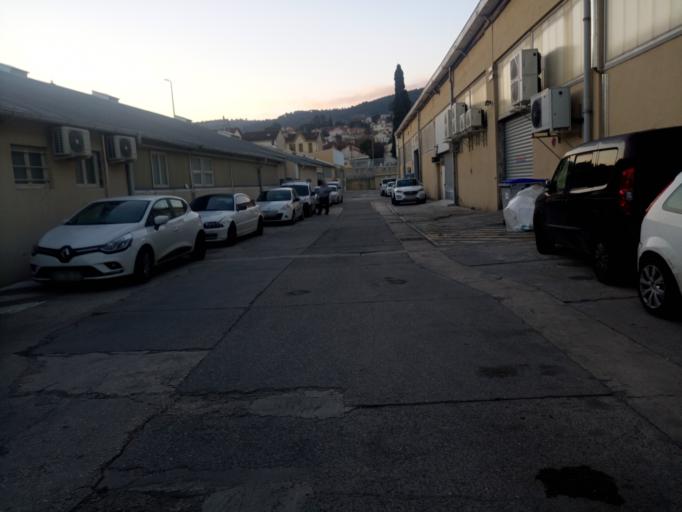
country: FR
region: Provence-Alpes-Cote d'Azur
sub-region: Departement des Bouches-du-Rhone
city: La Penne-sur-Huveaune
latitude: 43.2843
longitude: 5.4989
